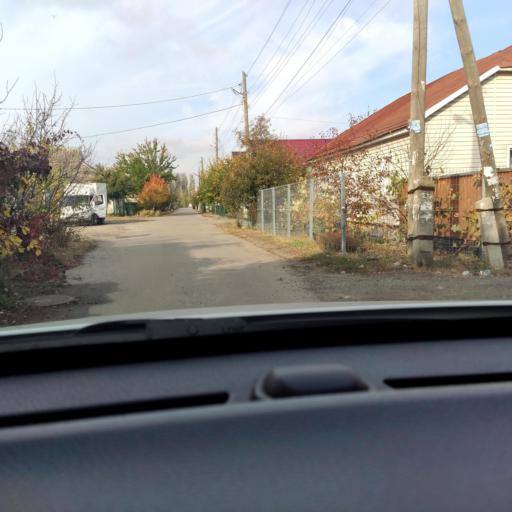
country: RU
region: Voronezj
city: Voronezh
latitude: 51.6320
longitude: 39.1640
